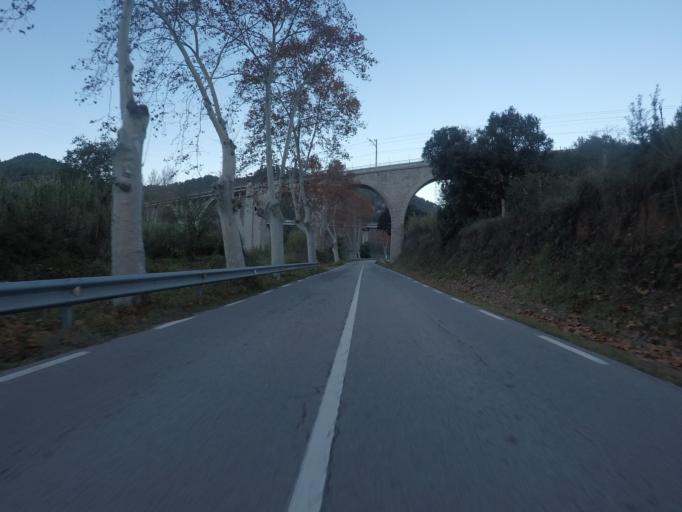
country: ES
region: Catalonia
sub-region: Provincia de Barcelona
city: Monistrol de Montserrat
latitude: 41.6210
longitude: 1.8541
